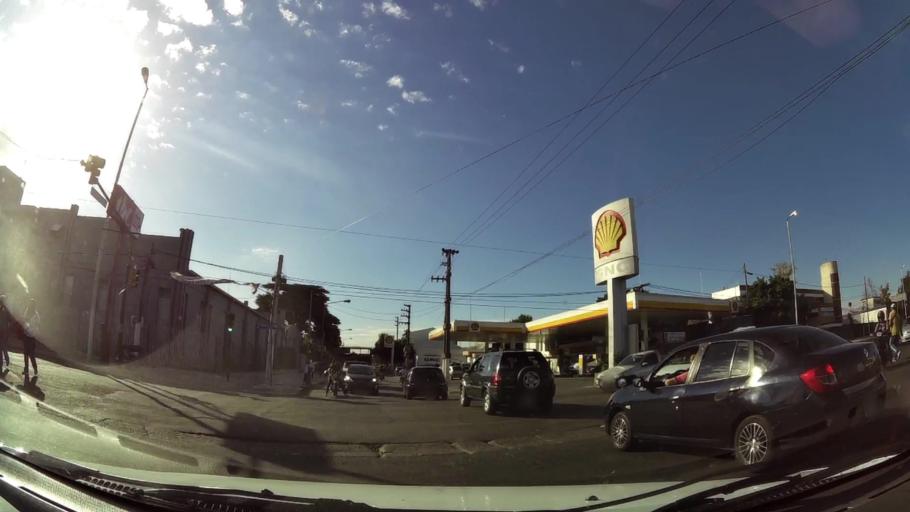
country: AR
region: Buenos Aires
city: Caseros
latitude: -34.5752
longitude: -58.5969
